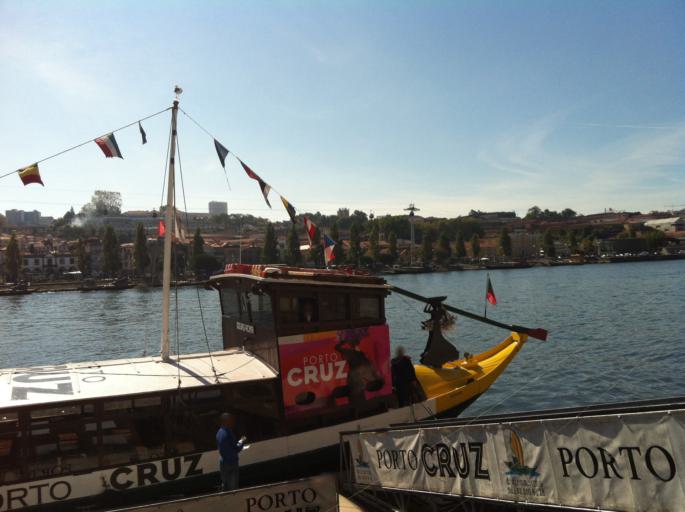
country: PT
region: Porto
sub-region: Vila Nova de Gaia
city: Vila Nova de Gaia
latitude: 41.1403
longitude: -8.6131
